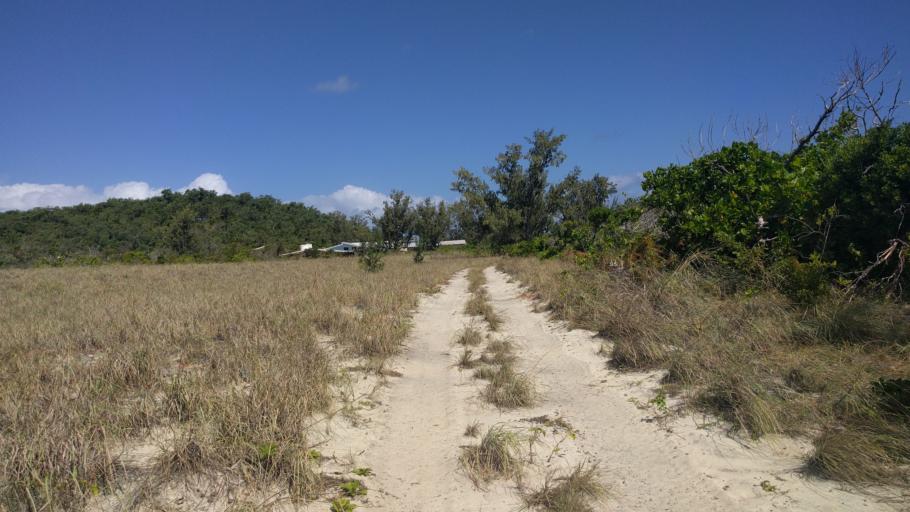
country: AU
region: Queensland
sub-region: Cook
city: Cooktown
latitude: -14.6771
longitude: 145.4474
